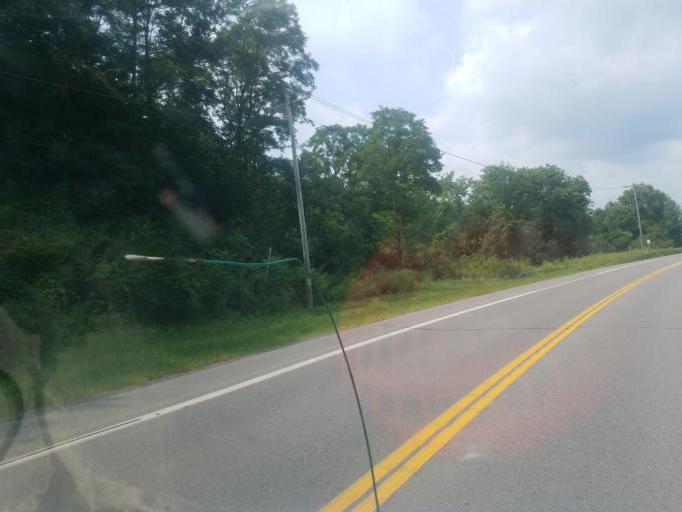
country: US
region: New York
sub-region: Herkimer County
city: Herkimer
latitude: 43.0132
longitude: -74.9459
